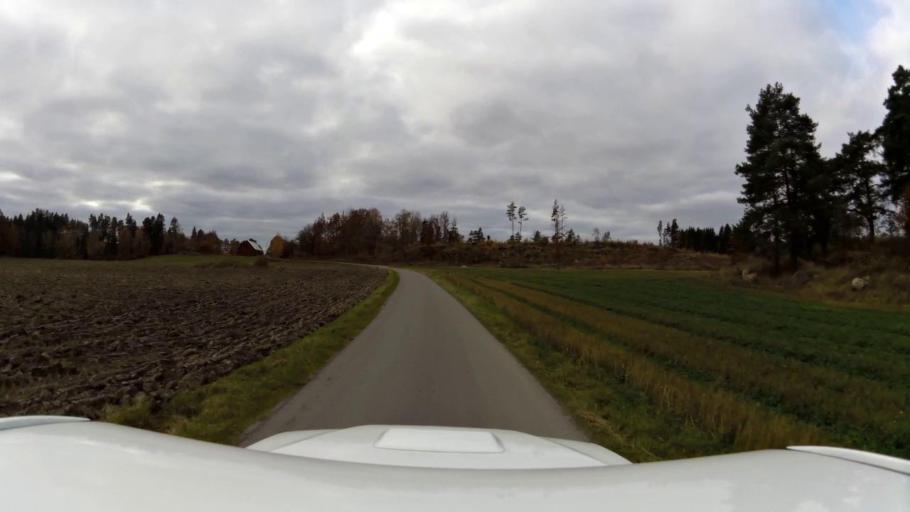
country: SE
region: OEstergoetland
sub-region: Linkopings Kommun
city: Linghem
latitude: 58.3821
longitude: 15.8303
